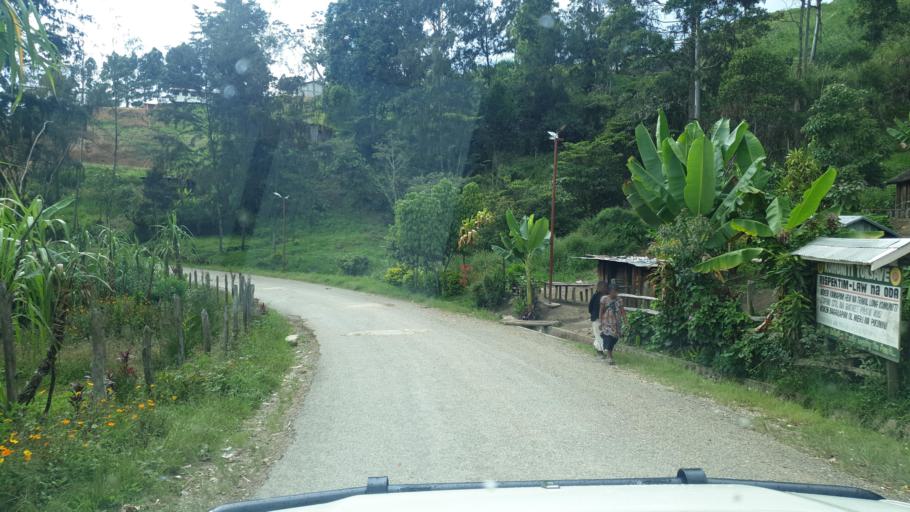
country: PG
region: Chimbu
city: Kundiawa
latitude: -6.1673
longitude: 145.1351
